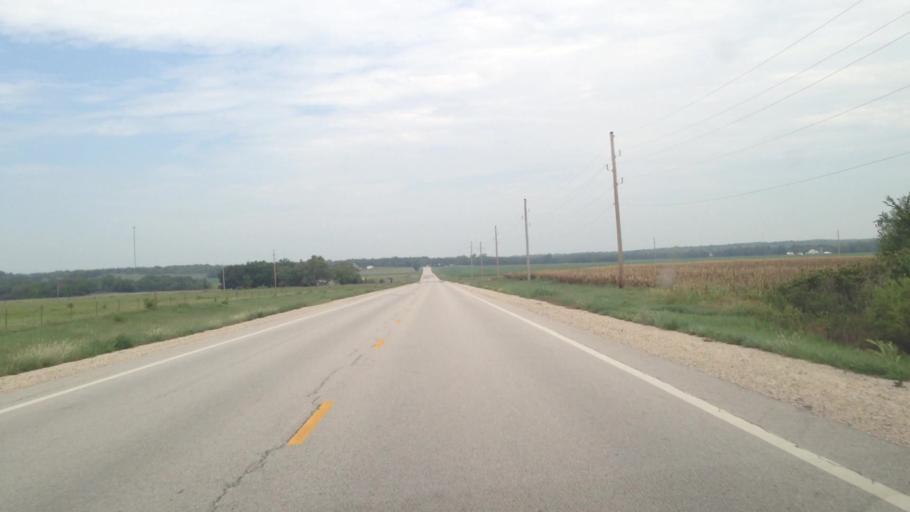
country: US
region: Kansas
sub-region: Anderson County
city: Garnett
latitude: 38.0631
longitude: -95.1693
